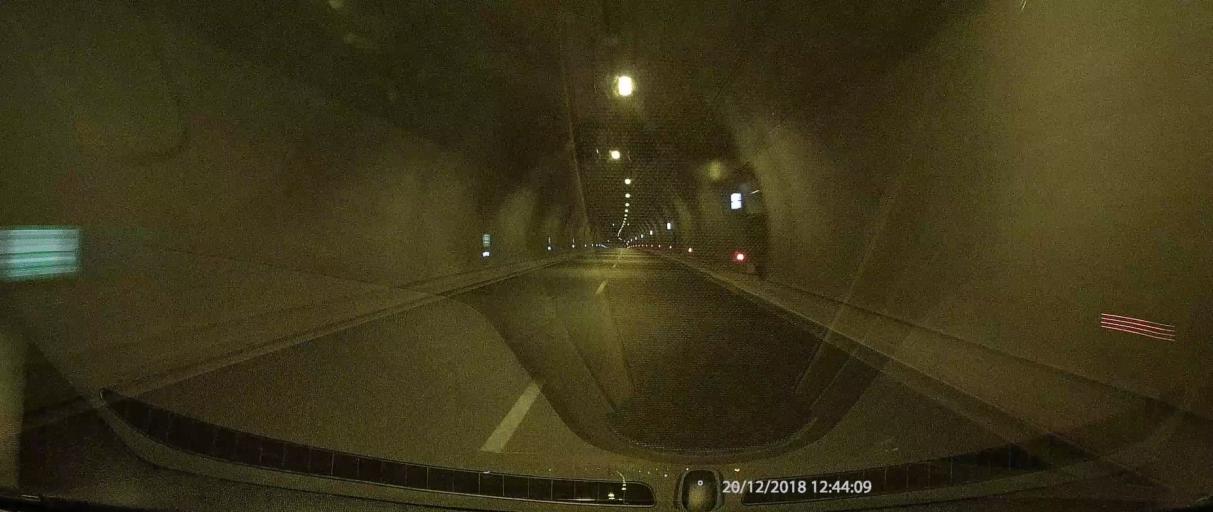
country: GR
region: West Greece
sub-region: Nomos Aitolias kai Akarnanias
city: Galatas
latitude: 38.3798
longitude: 21.5303
